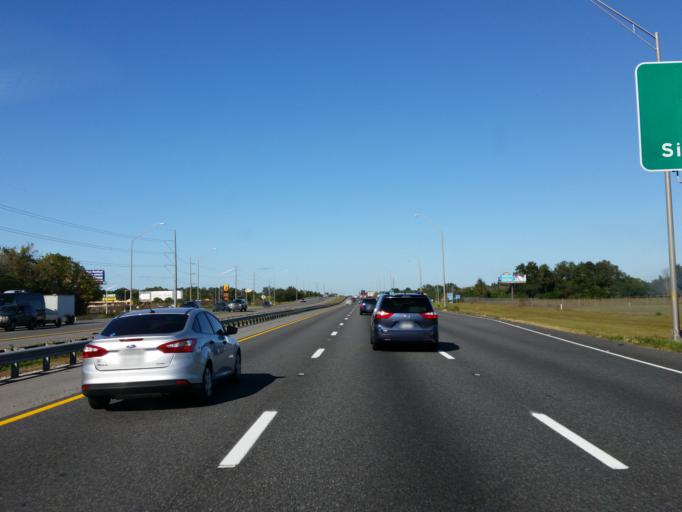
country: US
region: Florida
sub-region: Marion County
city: Ocala
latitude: 29.1809
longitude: -82.1847
